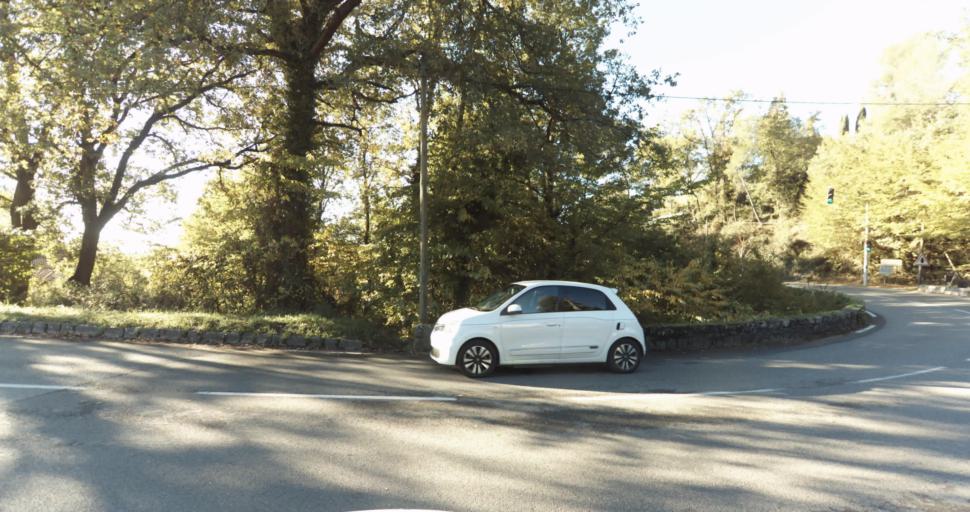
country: FR
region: Provence-Alpes-Cote d'Azur
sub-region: Departement des Alpes-Maritimes
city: Tourrettes-sur-Loup
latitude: 43.7238
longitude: 7.0796
